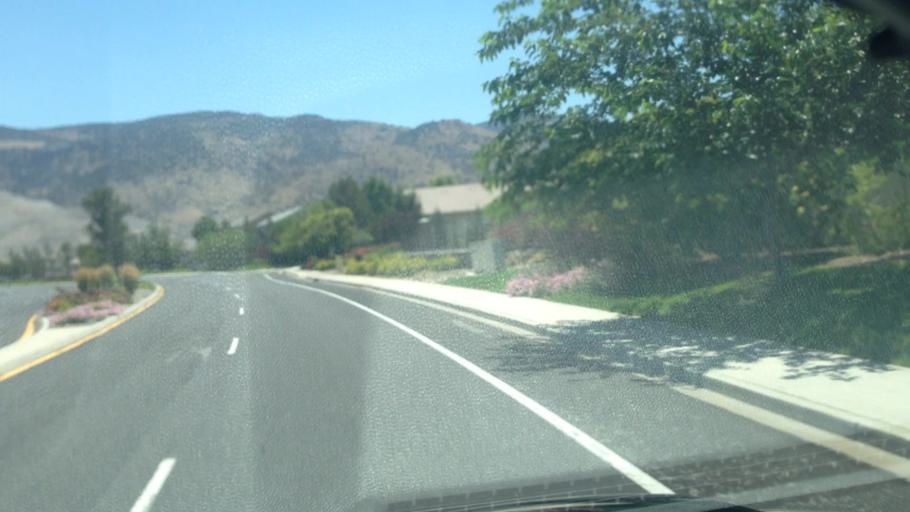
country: US
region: Nevada
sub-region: Washoe County
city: Sparks
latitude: 39.4152
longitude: -119.7302
